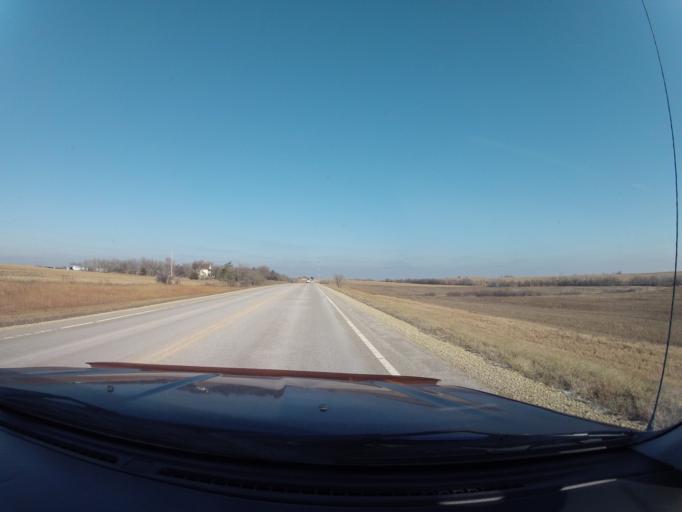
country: US
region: Kansas
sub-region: Marshall County
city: Blue Rapids
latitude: 39.5529
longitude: -96.7553
